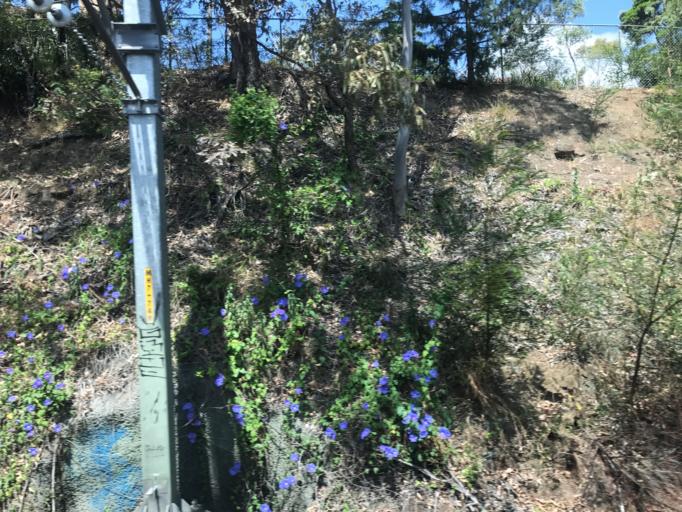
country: AU
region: New South Wales
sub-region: North Sydney
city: St Leonards
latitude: -33.8284
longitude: 151.1955
